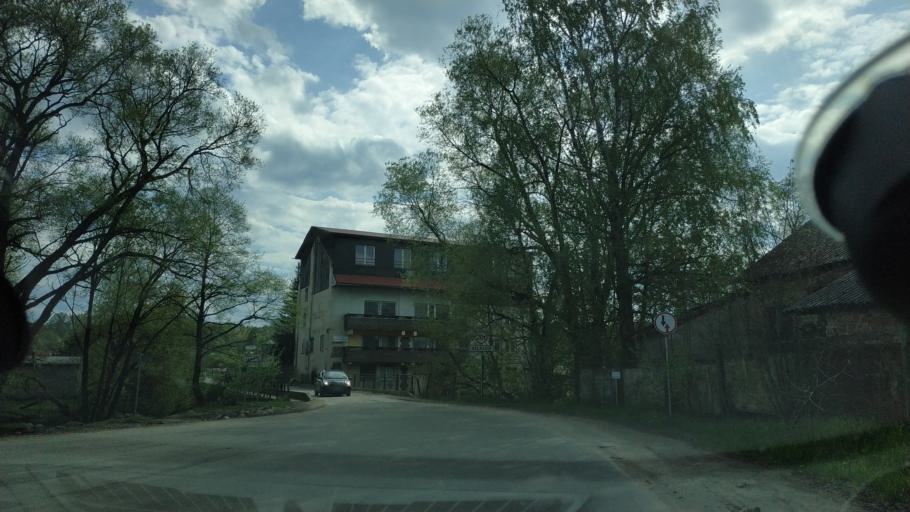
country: LT
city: Baltoji Voke
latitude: 54.5988
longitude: 25.1760
